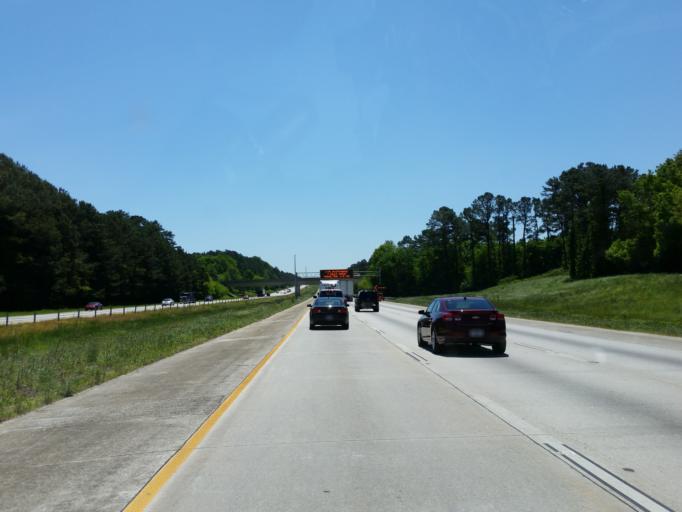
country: US
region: Georgia
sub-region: Clayton County
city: Conley
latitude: 33.6460
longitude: -84.3171
